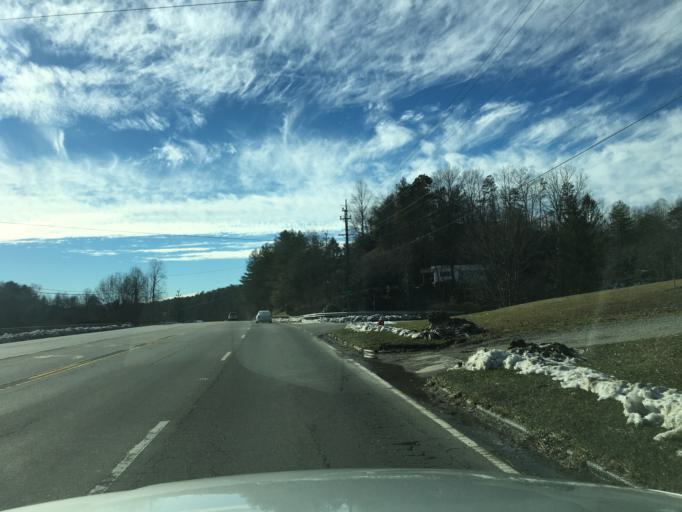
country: US
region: North Carolina
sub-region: Transylvania County
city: Brevard
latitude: 35.2154
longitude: -82.7558
